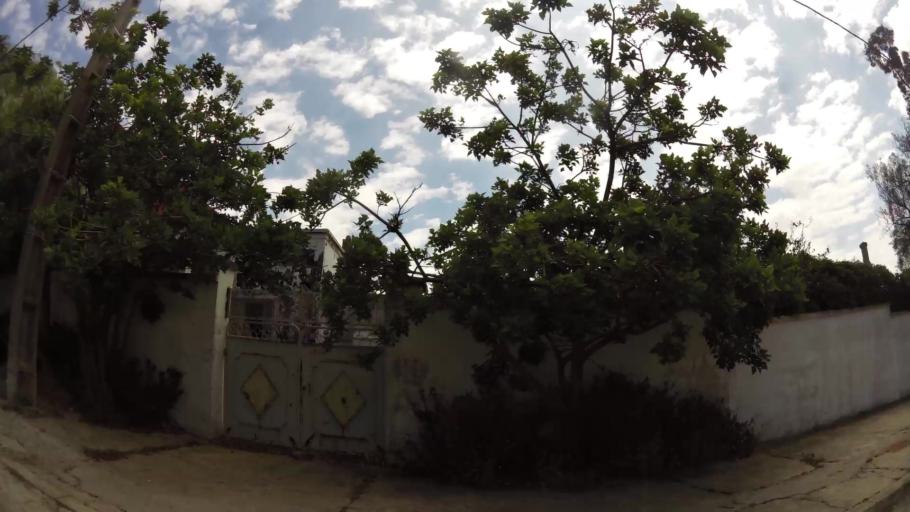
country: MA
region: Gharb-Chrarda-Beni Hssen
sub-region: Kenitra Province
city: Kenitra
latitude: 34.2639
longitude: -6.5983
